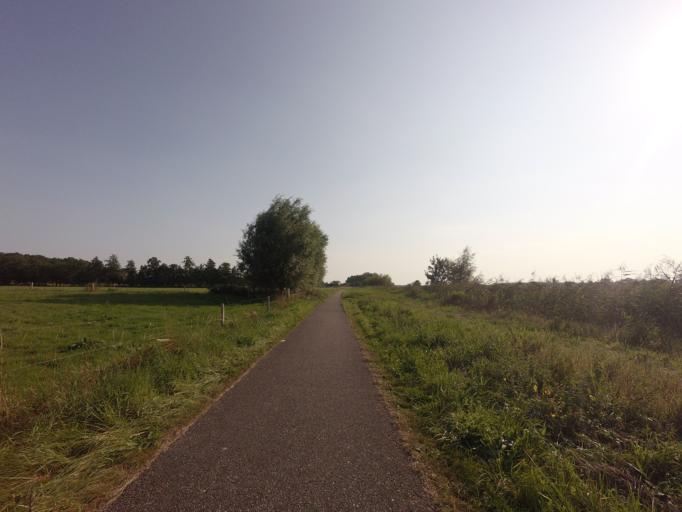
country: NL
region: Groningen
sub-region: Gemeente Zuidhorn
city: Aduard
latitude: 53.1677
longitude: 6.4876
